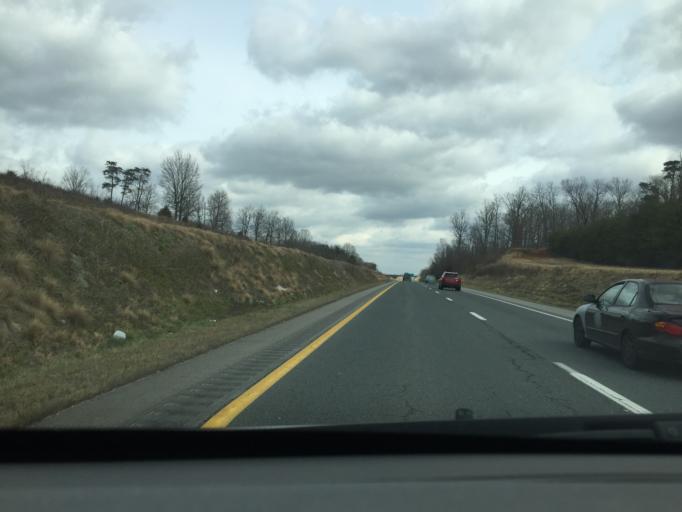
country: US
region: Virginia
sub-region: Campbell County
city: Timberlake
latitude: 37.3231
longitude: -79.2163
